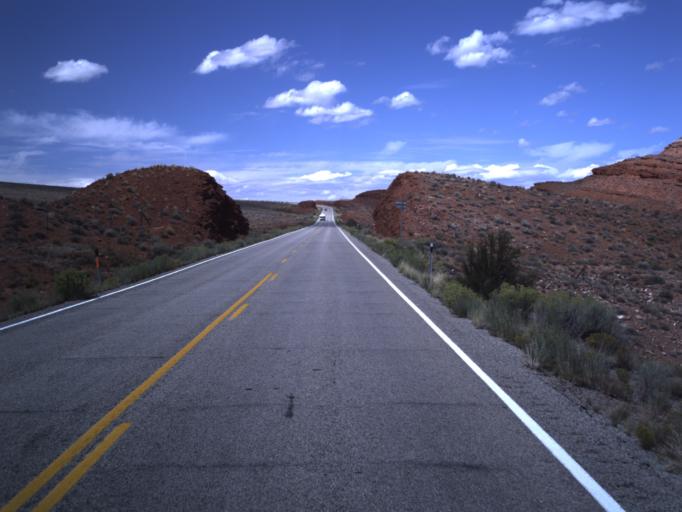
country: US
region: Utah
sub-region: San Juan County
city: Blanding
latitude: 37.2783
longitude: -109.6834
